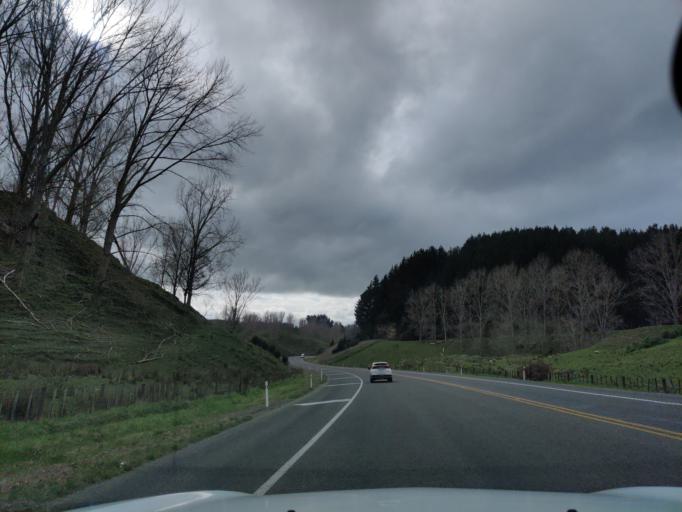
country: NZ
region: Manawatu-Wanganui
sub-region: Rangitikei District
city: Bulls
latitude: -39.9262
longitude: 175.6141
